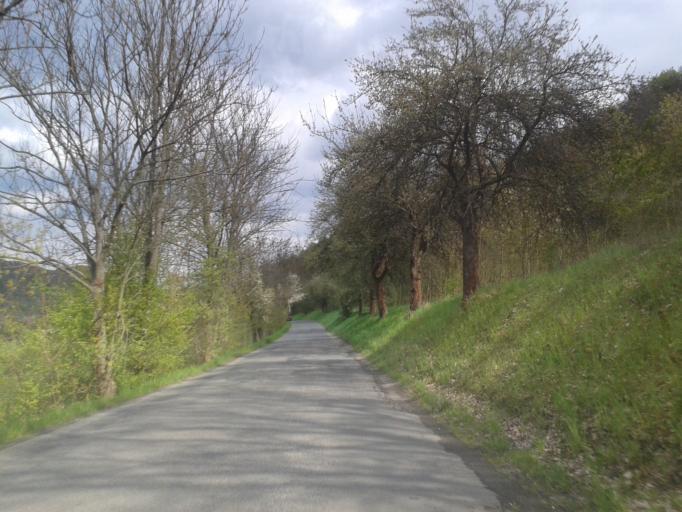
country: CZ
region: Central Bohemia
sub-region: Okres Beroun
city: Lodenice
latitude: 49.9287
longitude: 14.1690
